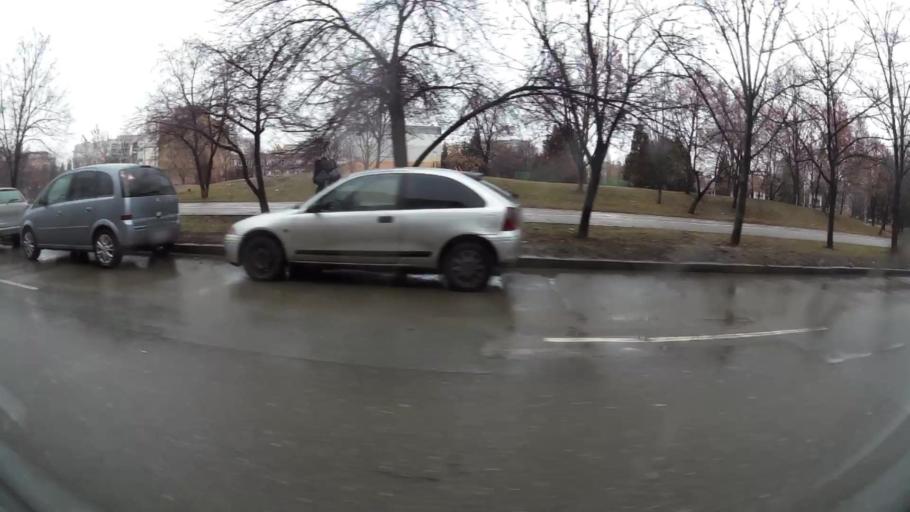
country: BG
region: Sofia-Capital
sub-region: Stolichna Obshtina
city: Sofia
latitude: 42.6406
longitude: 23.3788
